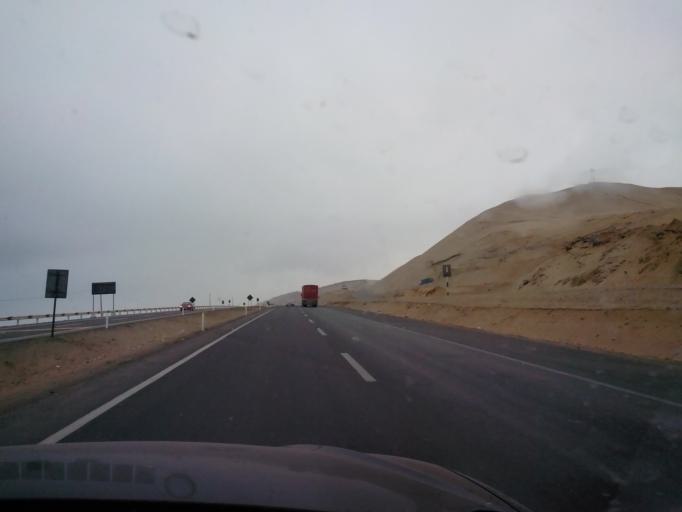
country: PE
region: Ica
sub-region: Provincia de Chincha
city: San Pedro
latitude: -13.3192
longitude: -76.2453
